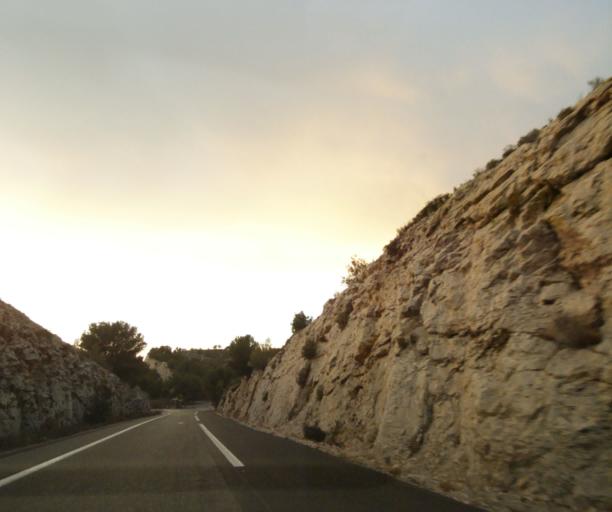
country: FR
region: Provence-Alpes-Cote d'Azur
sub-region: Departement des Bouches-du-Rhone
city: Sausset-les-Pins
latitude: 43.3419
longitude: 5.1073
